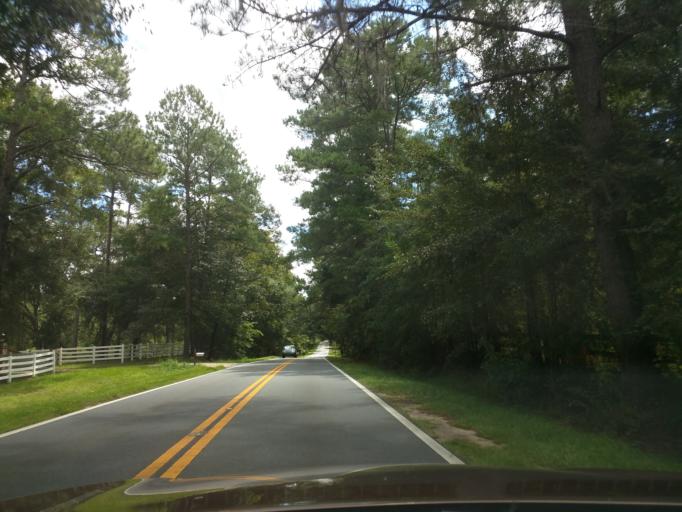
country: US
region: Florida
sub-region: Leon County
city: Tallahassee
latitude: 30.5592
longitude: -84.1828
